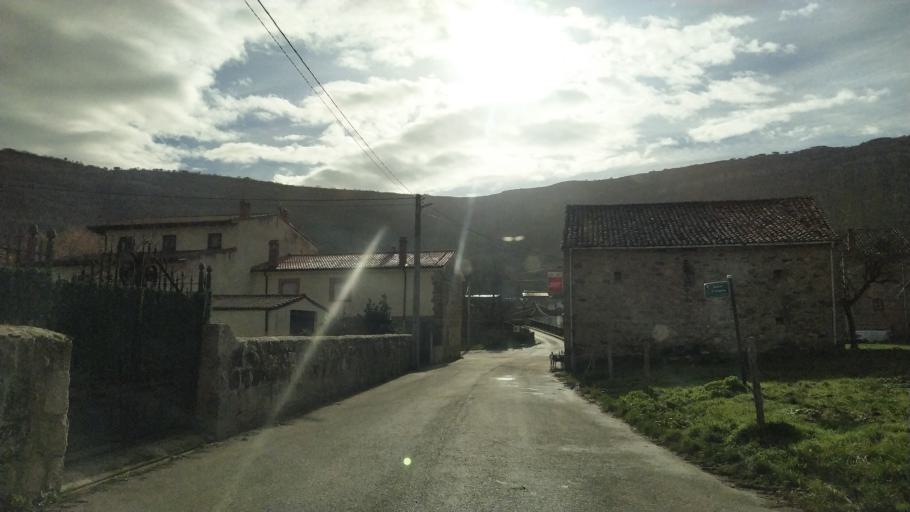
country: ES
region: Cantabria
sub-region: Provincia de Cantabria
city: San Martin de Elines
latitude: 42.8337
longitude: -3.8611
